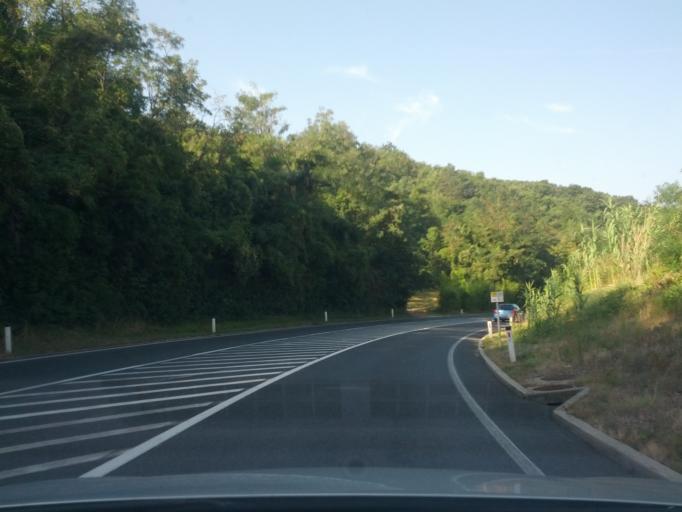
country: SI
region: Koper-Capodistria
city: Koper
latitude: 45.5072
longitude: 13.7047
